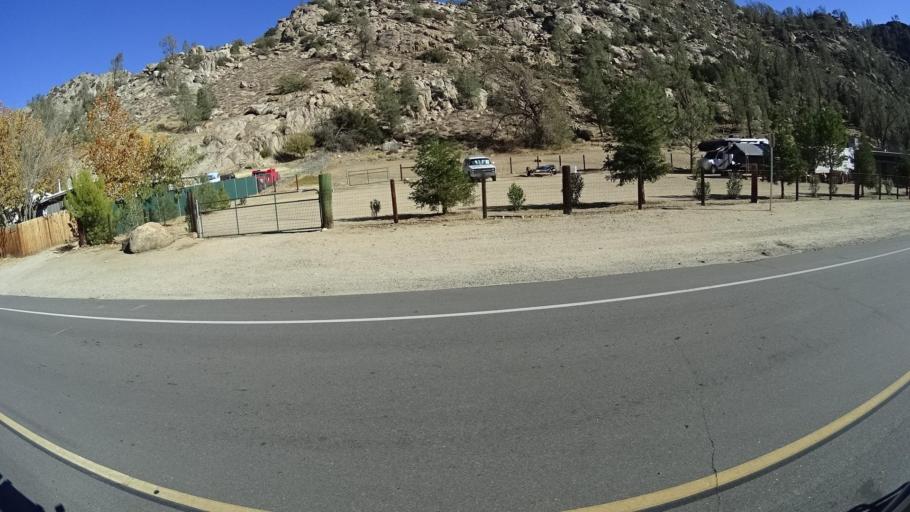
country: US
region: California
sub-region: Kern County
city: Kernville
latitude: 35.7376
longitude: -118.4146
